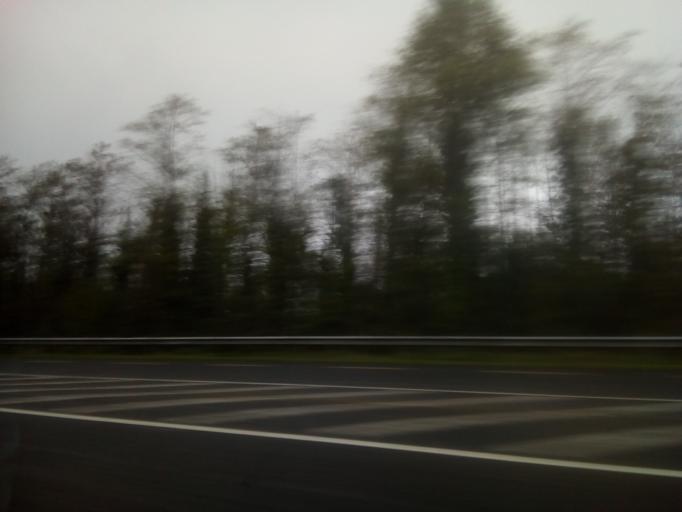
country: IE
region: Leinster
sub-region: An Iarmhi
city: An Muileann gCearr
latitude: 53.5537
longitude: -7.3409
